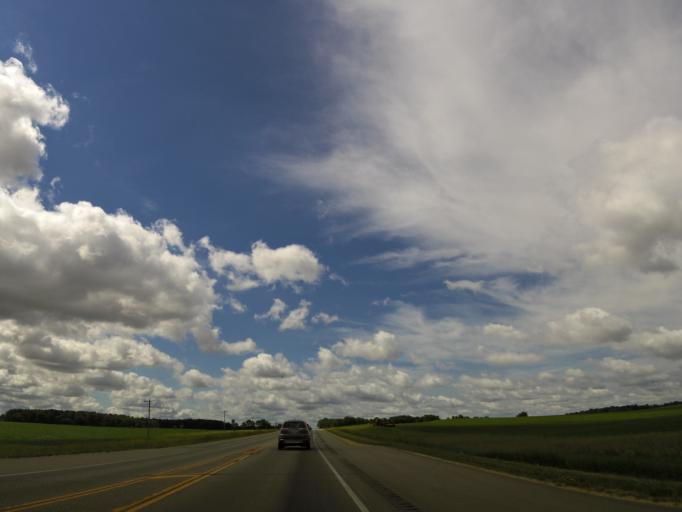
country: US
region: Minnesota
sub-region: Mower County
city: Grand Meadow
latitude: 43.7385
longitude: -92.4794
